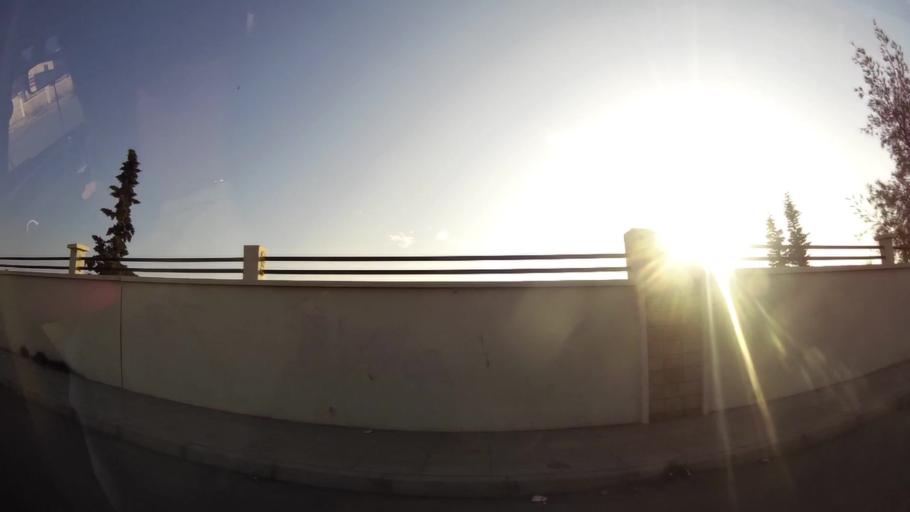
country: MA
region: Oriental
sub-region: Oujda-Angad
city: Oujda
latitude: 34.6722
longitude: -1.9361
